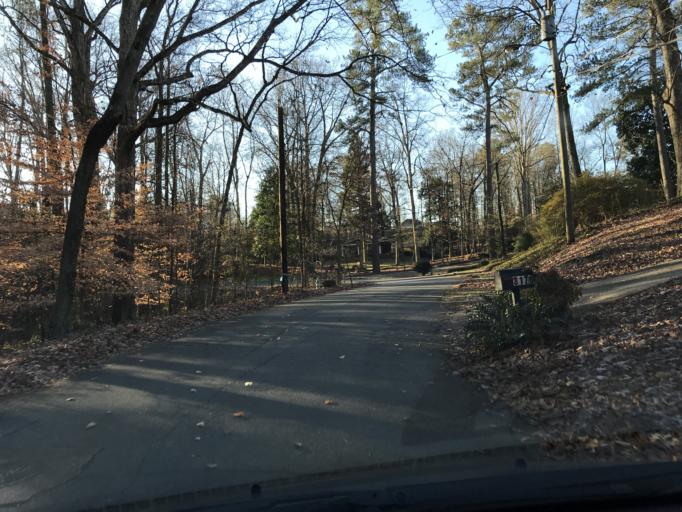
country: US
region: Georgia
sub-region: DeKalb County
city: North Atlanta
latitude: 33.8824
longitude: -84.3312
